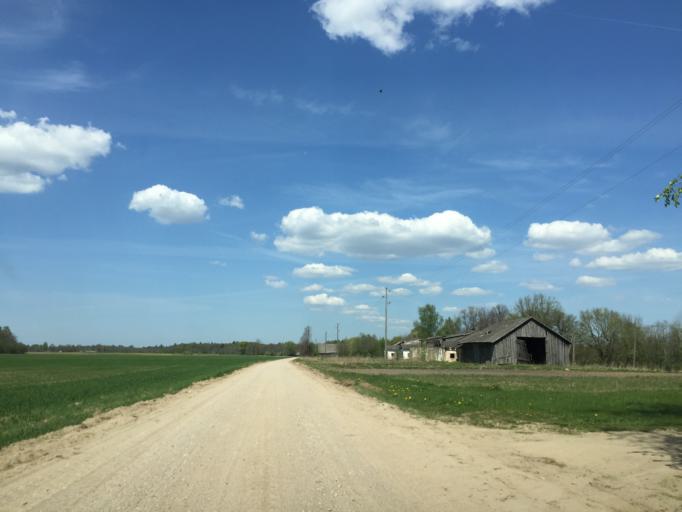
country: LV
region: Limbazu Rajons
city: Limbazi
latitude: 57.3705
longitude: 24.6339
